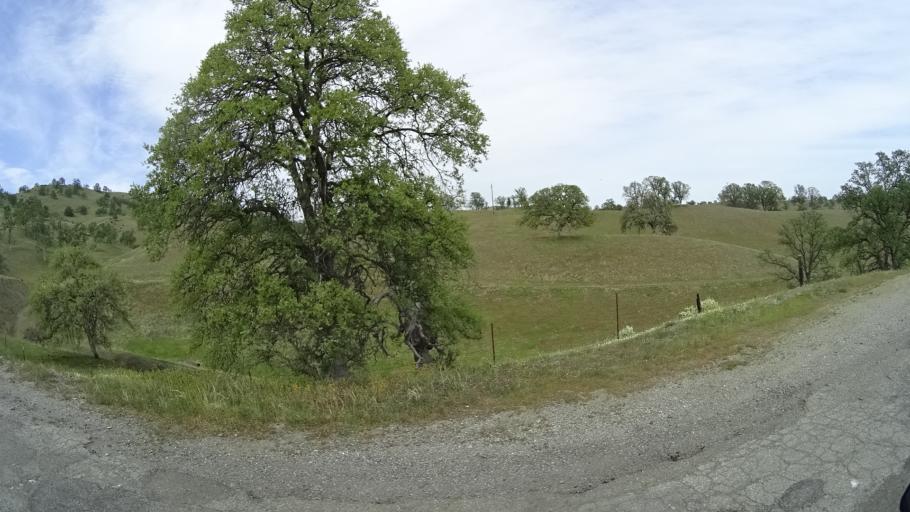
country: US
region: California
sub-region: Glenn County
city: Willows
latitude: 39.6120
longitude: -122.5776
